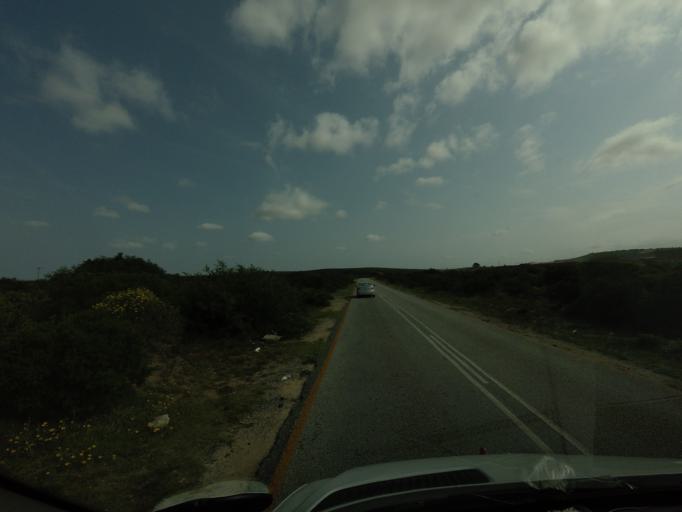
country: ZA
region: Eastern Cape
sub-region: Nelson Mandela Bay Metropolitan Municipality
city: Port Elizabeth
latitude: -33.7406
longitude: 25.5922
